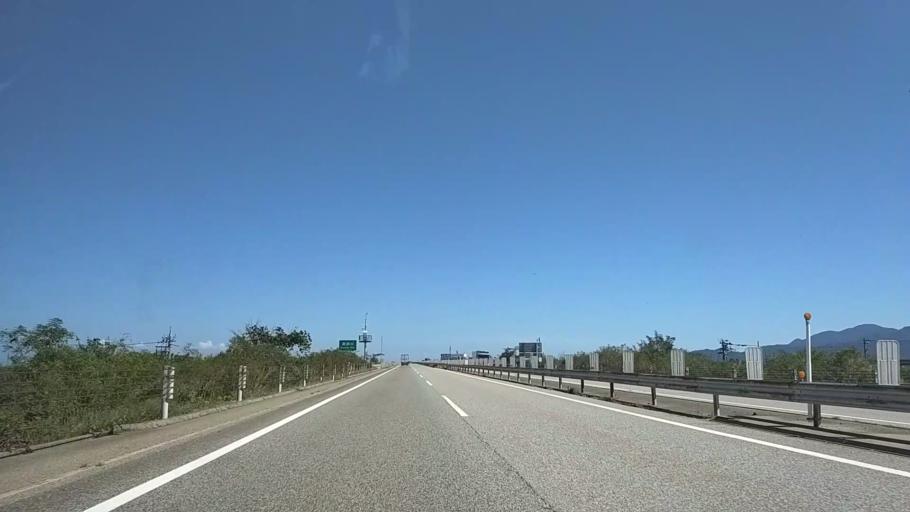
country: JP
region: Toyama
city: Nyuzen
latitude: 36.8892
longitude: 137.4906
